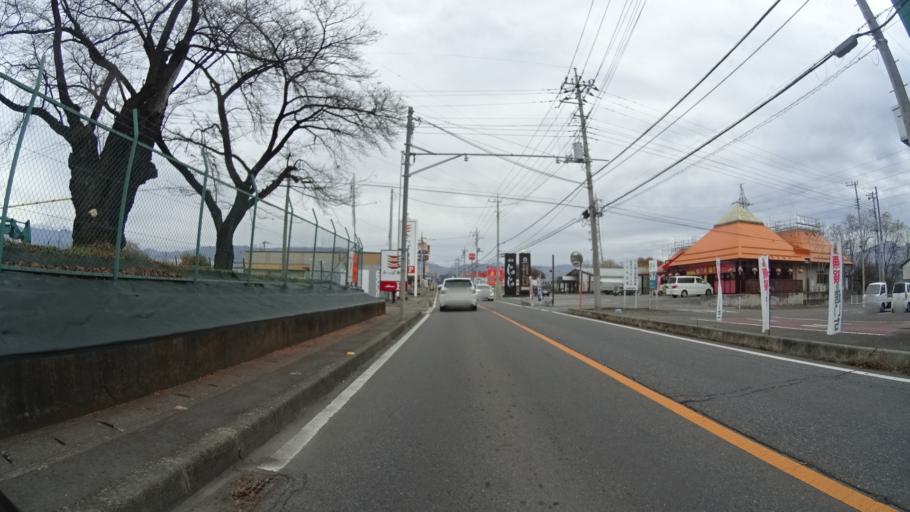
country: JP
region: Gunma
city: Numata
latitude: 36.6572
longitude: 139.0790
